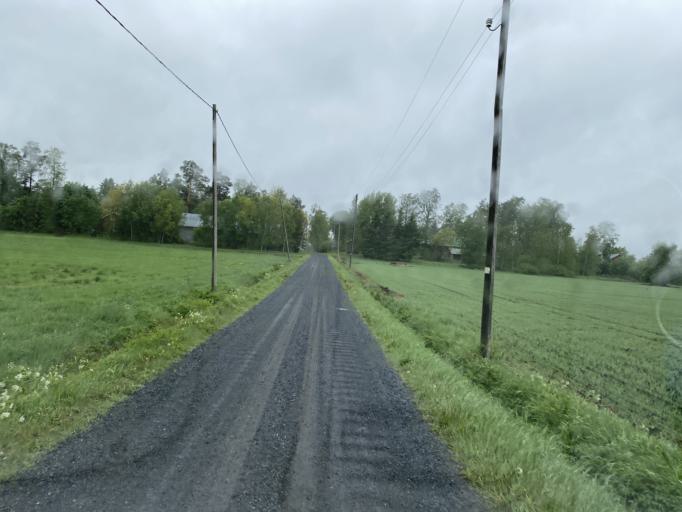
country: FI
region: Pirkanmaa
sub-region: Etelae-Pirkanmaa
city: Urjala
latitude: 60.9504
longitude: 23.5498
